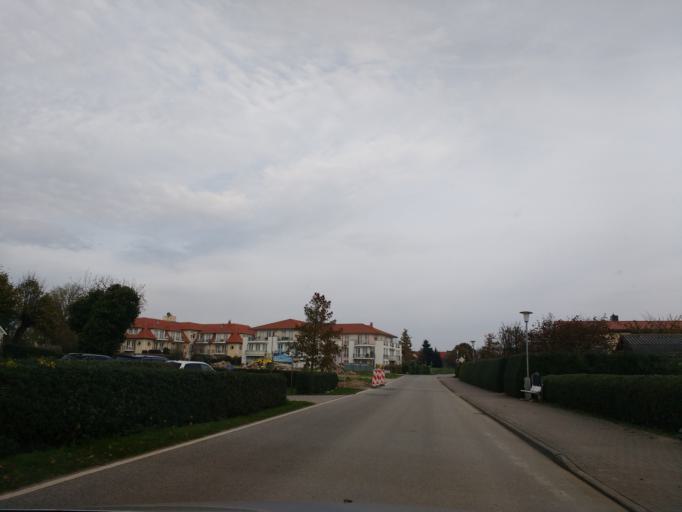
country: DE
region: Mecklenburg-Vorpommern
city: Ostseebad Boltenhagen
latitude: 53.9971
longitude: 11.1883
